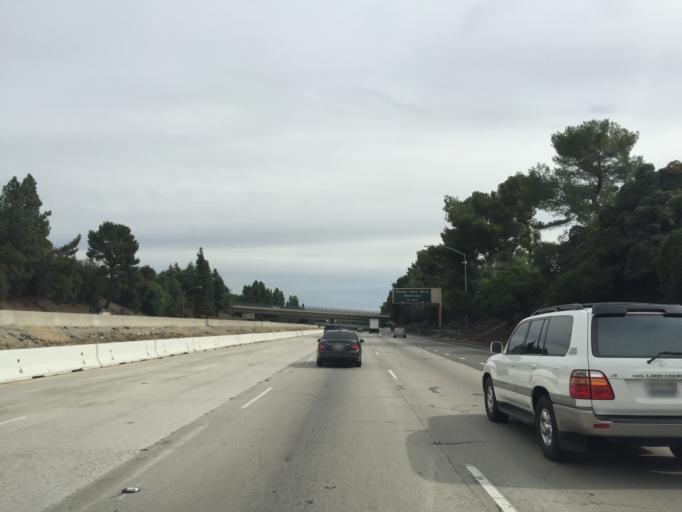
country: US
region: California
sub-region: Los Angeles County
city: La Crescenta-Montrose
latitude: 34.2177
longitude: -118.2384
